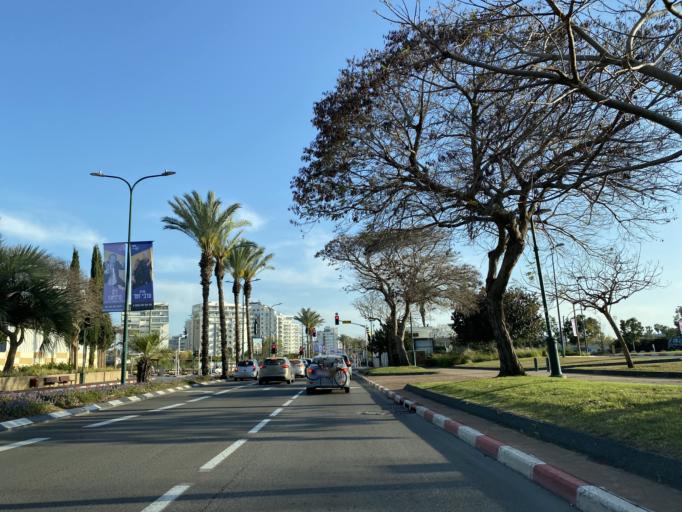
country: IL
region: Tel Aviv
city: Herzliyya
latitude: 32.1695
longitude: 34.8287
